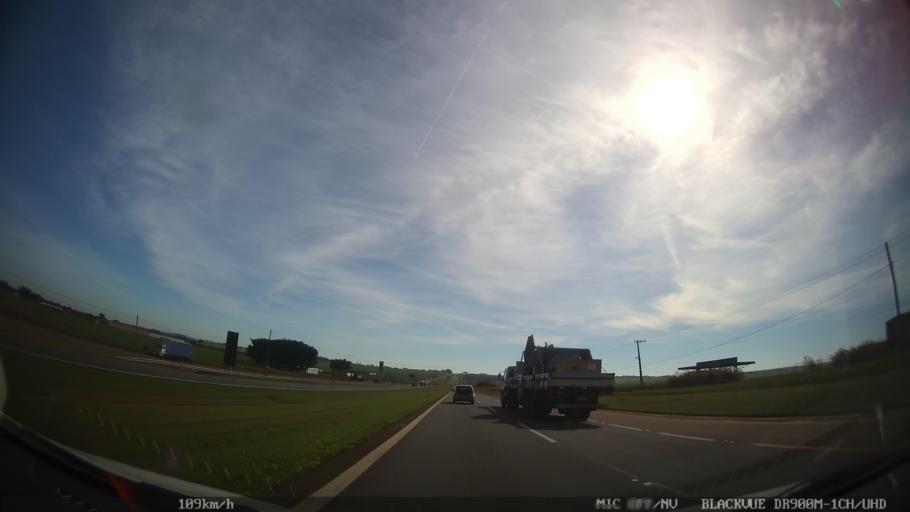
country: BR
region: Sao Paulo
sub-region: Cordeiropolis
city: Cordeiropolis
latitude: -22.4892
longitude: -47.3992
